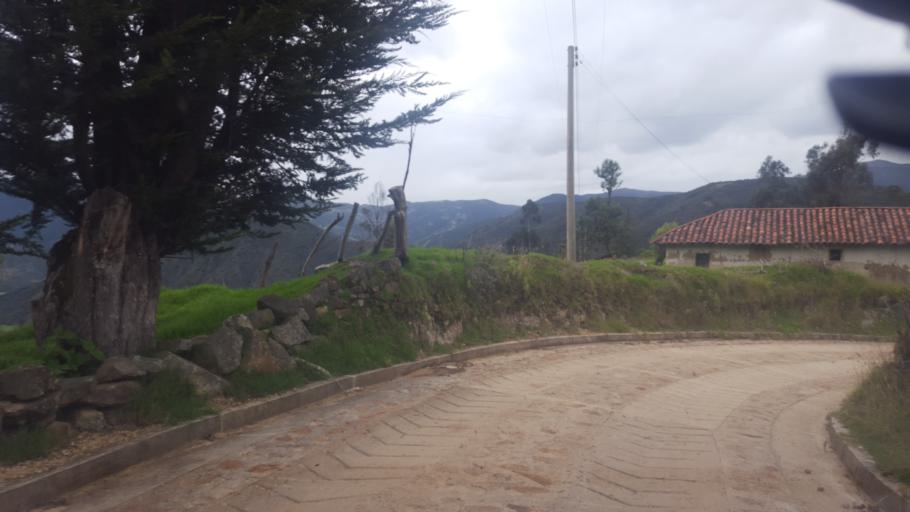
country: CO
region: Boyaca
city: Belen
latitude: 6.0215
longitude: -72.8775
